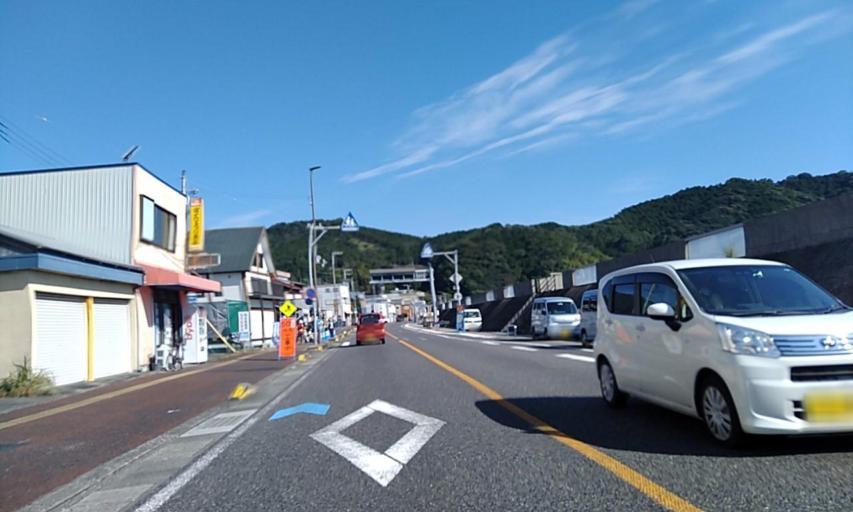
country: JP
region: Wakayama
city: Shingu
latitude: 33.8892
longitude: 136.1037
